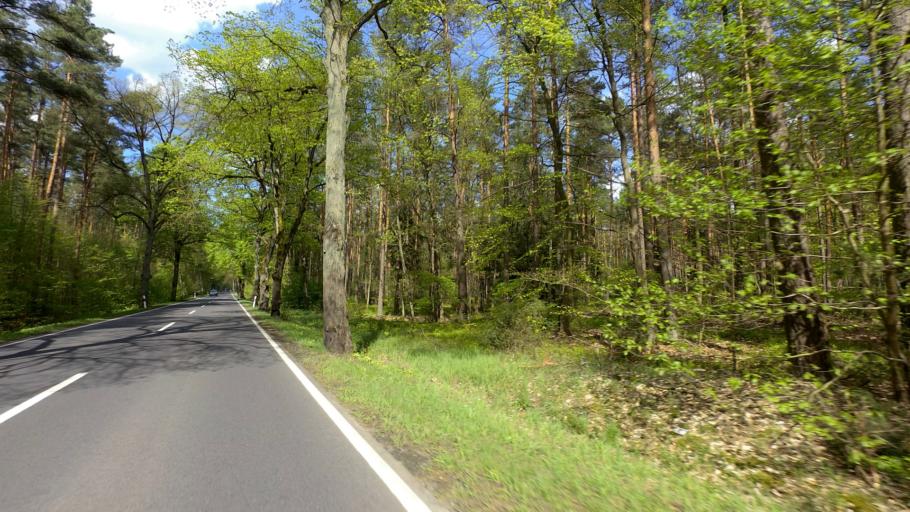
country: DE
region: Brandenburg
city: Milmersdorf
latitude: 53.0161
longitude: 13.6019
